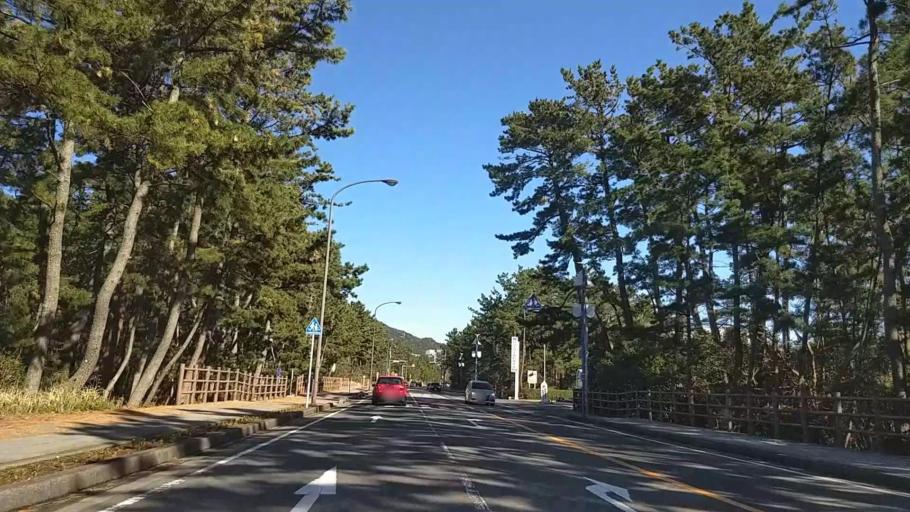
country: JP
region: Chiba
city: Kawaguchi
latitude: 35.1142
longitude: 140.1165
